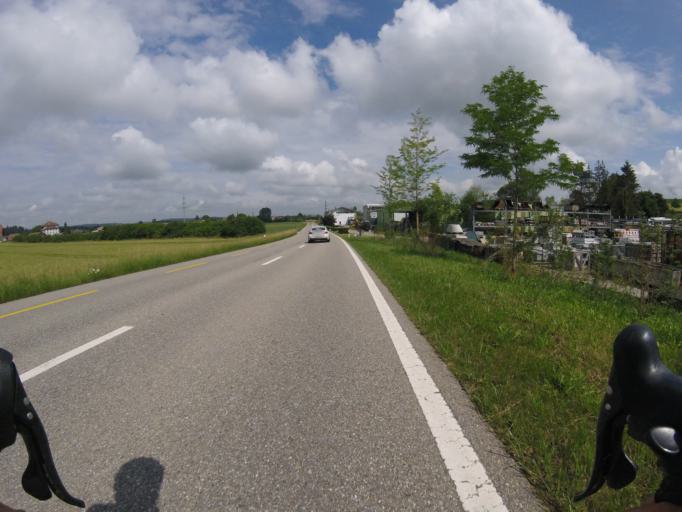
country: CH
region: Bern
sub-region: Emmental District
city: Hindelbank
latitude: 47.0348
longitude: 7.5486
